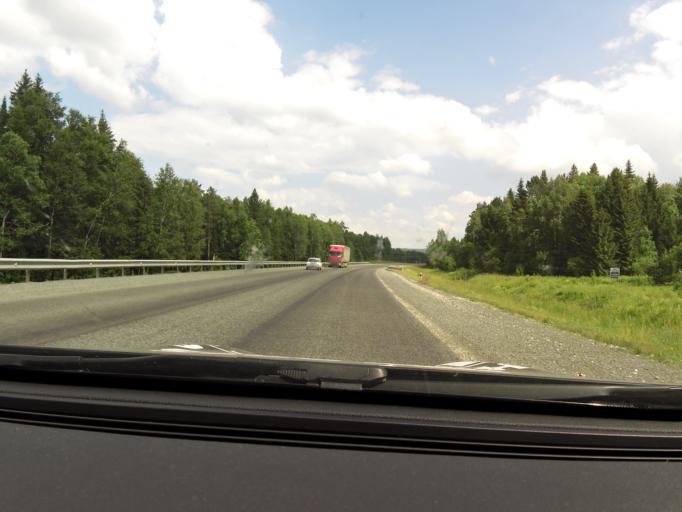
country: RU
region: Sverdlovsk
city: Ufimskiy
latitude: 56.7870
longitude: 58.3817
